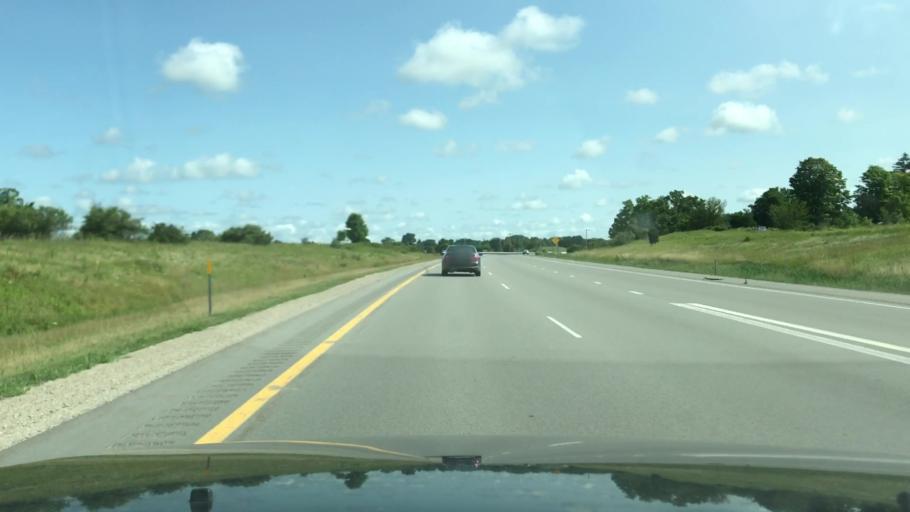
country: US
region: Michigan
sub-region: Kent County
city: Cedar Springs
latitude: 43.2253
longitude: -85.5737
